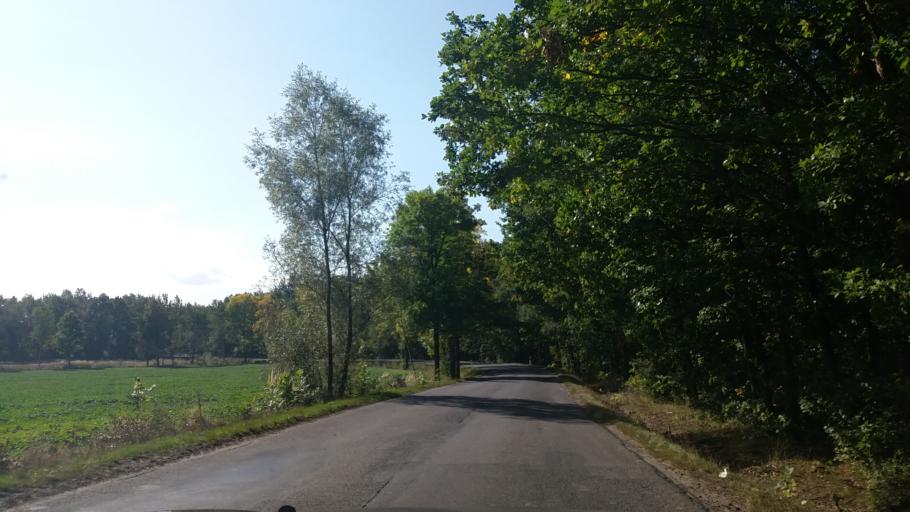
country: PL
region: Lower Silesian Voivodeship
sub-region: Powiat legnicki
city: Prochowice
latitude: 51.2389
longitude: 16.3613
